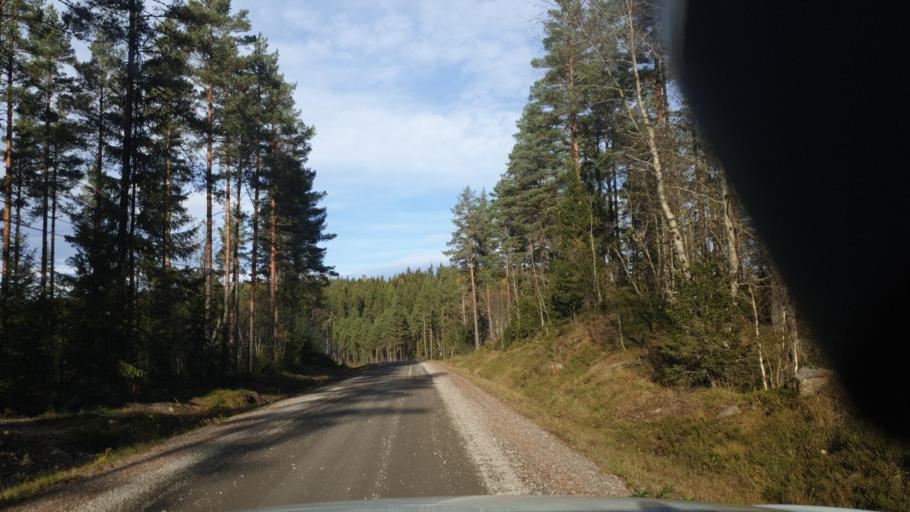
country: SE
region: Vaermland
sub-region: Eda Kommun
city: Charlottenberg
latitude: 59.9803
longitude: 12.4900
